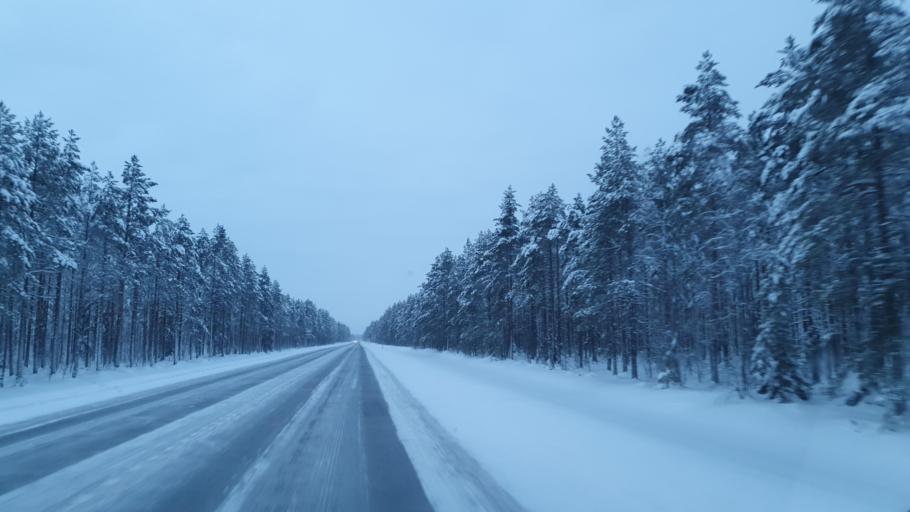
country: FI
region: Kainuu
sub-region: Kajaani
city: Vaala
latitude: 64.6021
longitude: 26.6609
